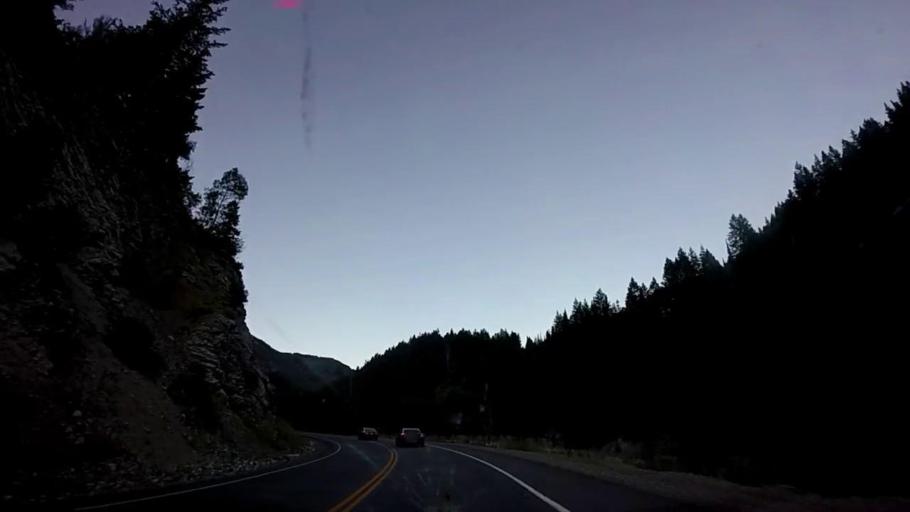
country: US
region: Utah
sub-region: Summit County
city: Summit Park
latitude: 40.6453
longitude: -111.6675
